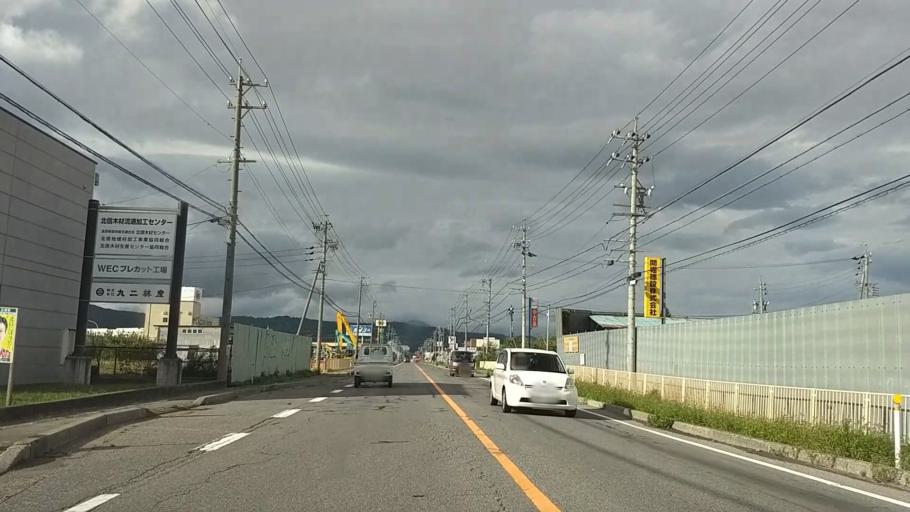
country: JP
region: Nagano
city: Suzaka
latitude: 36.6794
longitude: 138.2677
